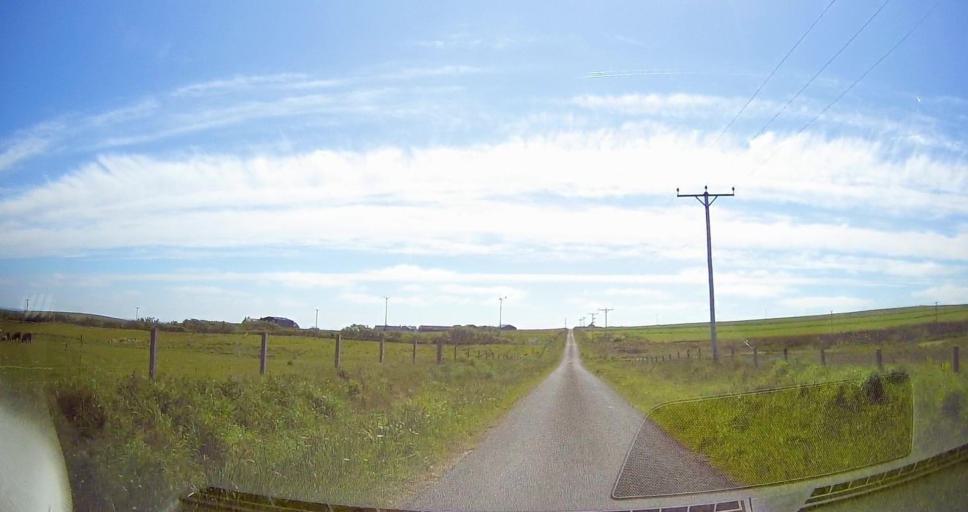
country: GB
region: Scotland
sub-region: Orkney Islands
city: Kirkwall
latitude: 58.8246
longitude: -2.9095
